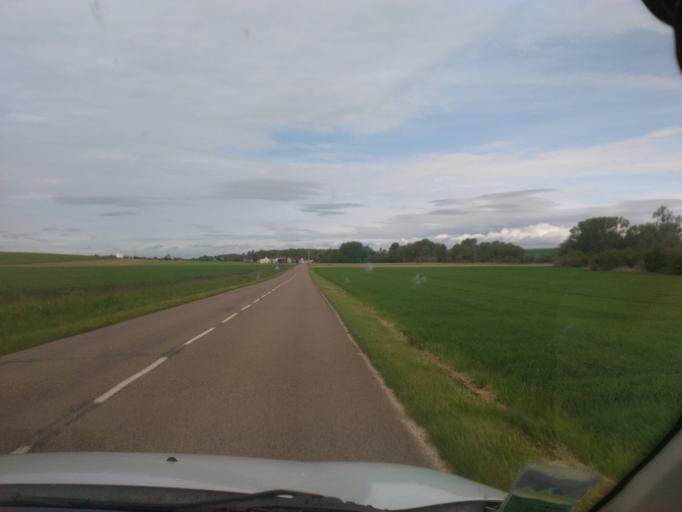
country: FR
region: Champagne-Ardenne
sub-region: Departement de l'Aube
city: Marigny-le-Chatel
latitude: 48.3542
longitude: 3.6701
